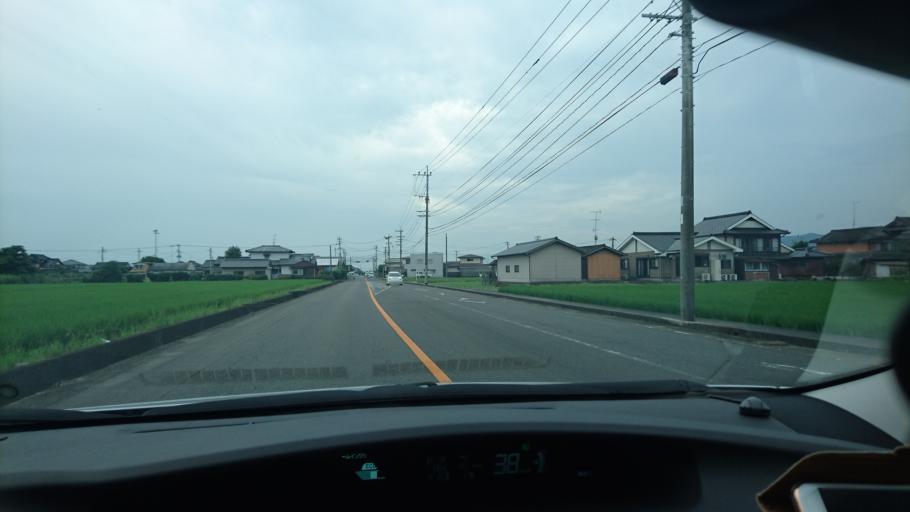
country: JP
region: Saga Prefecture
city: Takeocho-takeo
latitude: 33.2102
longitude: 130.1212
